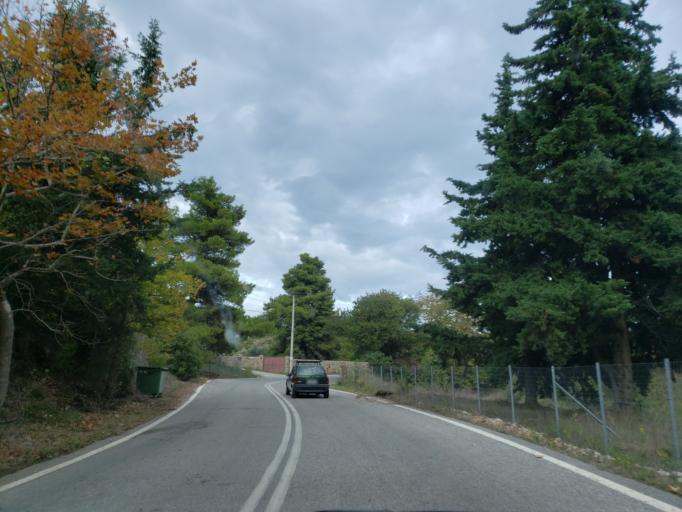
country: GR
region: Attica
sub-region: Nomarchia Anatolikis Attikis
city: Varnavas
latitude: 38.2194
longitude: 23.9350
